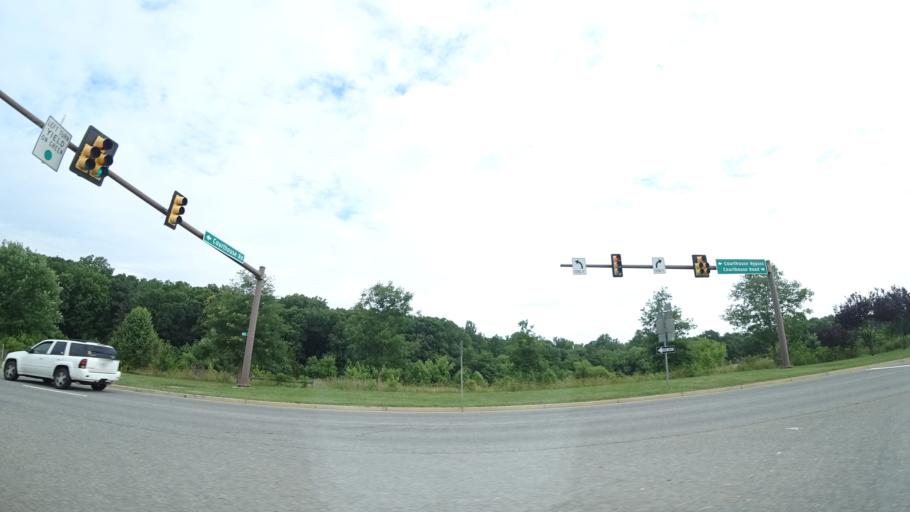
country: US
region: Virginia
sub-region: Spotsylvania County
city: Spotsylvania
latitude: 38.2081
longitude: -77.5817
